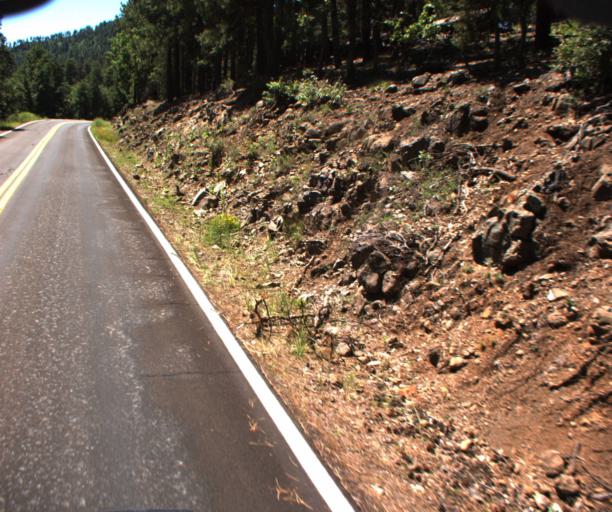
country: US
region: Arizona
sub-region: Greenlee County
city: Morenci
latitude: 33.4486
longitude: -109.3701
